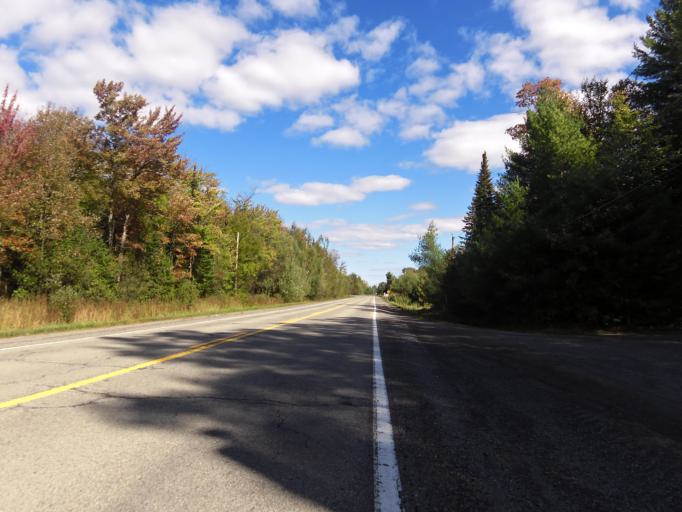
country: CA
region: Ontario
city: Ottawa
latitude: 45.3625
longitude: -75.5279
